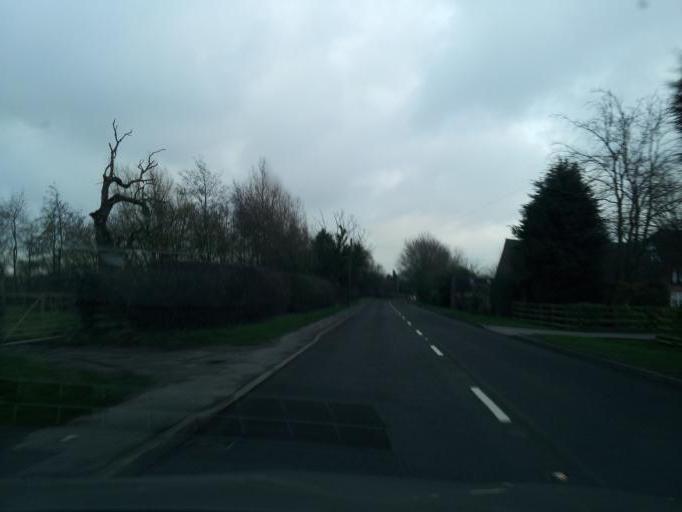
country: GB
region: England
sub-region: Derbyshire
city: Etwall
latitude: 52.8680
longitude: -1.6188
